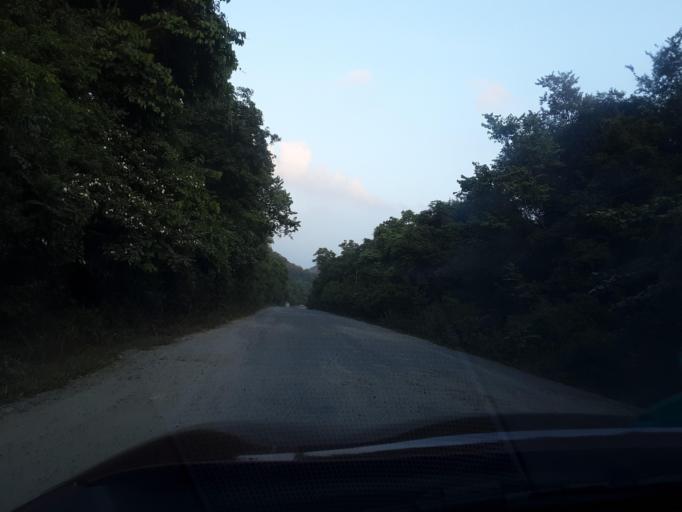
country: LK
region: Central
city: Dambulla
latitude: 7.8103
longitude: 80.7738
